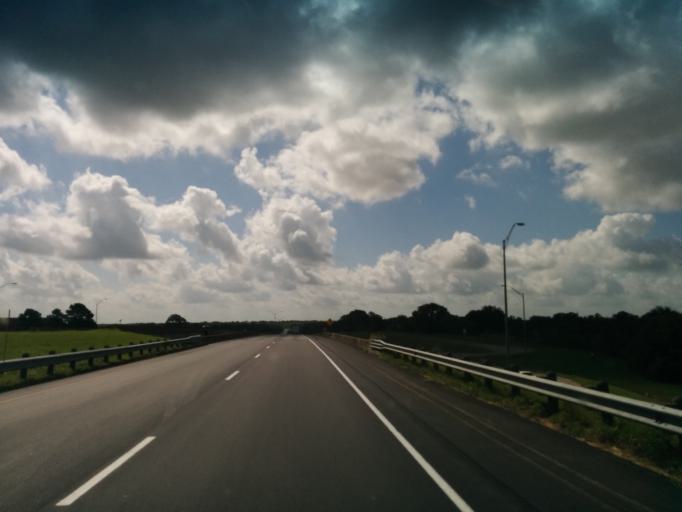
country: US
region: Texas
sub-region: Fayette County
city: Schulenburg
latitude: 29.6945
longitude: -96.8500
